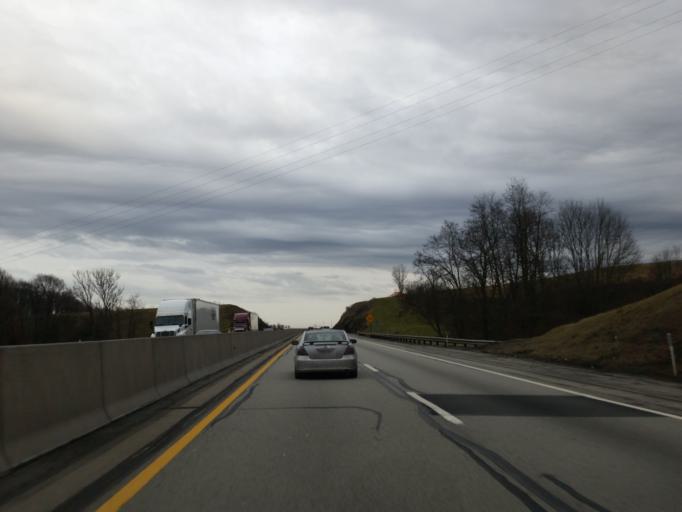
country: US
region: Pennsylvania
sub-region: Somerset County
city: Somerset
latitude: 40.0494
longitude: -79.1239
